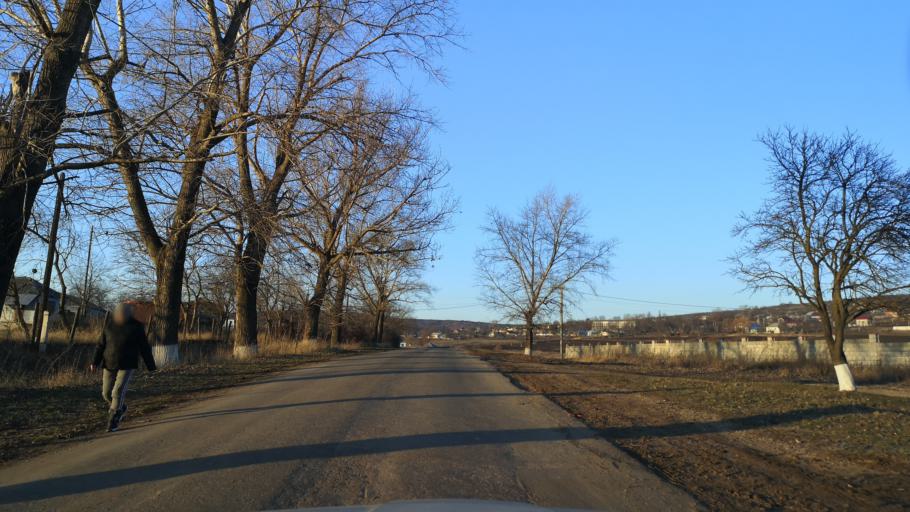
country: MD
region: Orhei
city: Orhei
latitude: 47.3482
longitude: 28.6967
